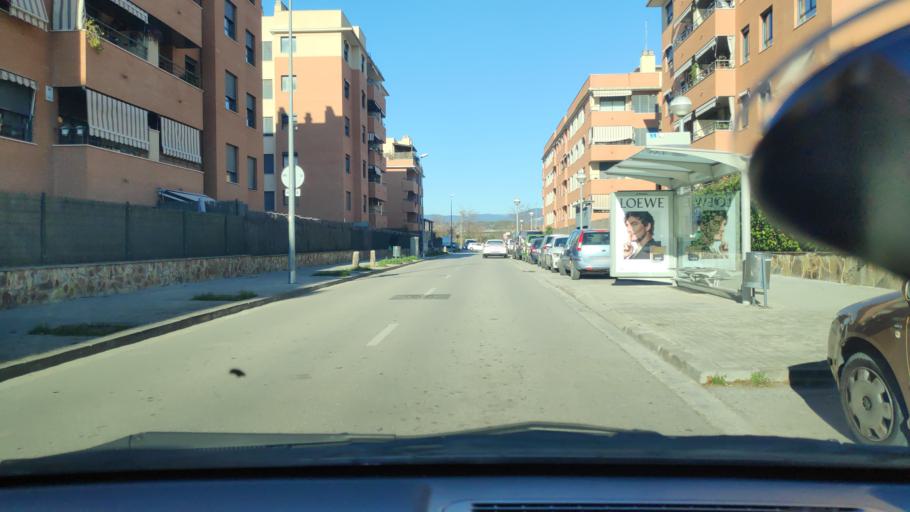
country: ES
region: Catalonia
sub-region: Provincia de Barcelona
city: Sant Quirze del Valles
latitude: 41.5624
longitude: 2.0762
